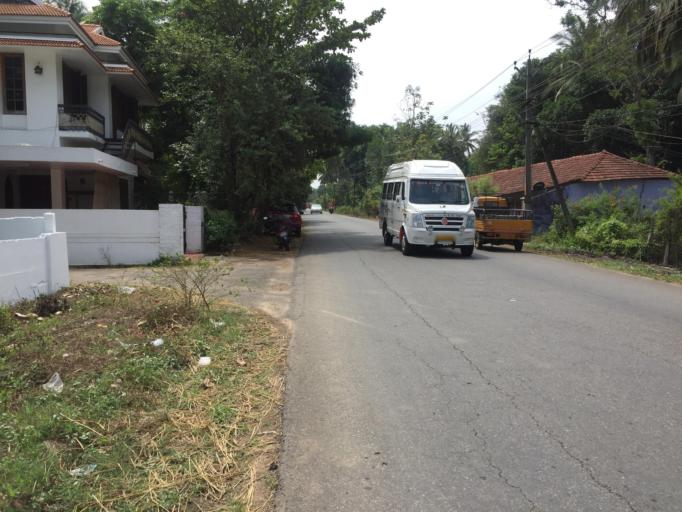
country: IN
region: Kerala
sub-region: Palakkad district
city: Chittur
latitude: 10.6803
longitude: 76.7163
